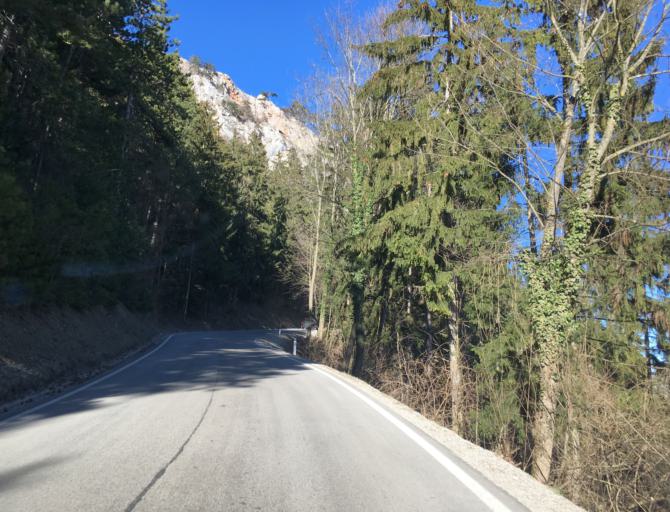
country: AT
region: Lower Austria
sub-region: Politischer Bezirk Wiener Neustadt
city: Waldegg
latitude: 47.8327
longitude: 16.0559
